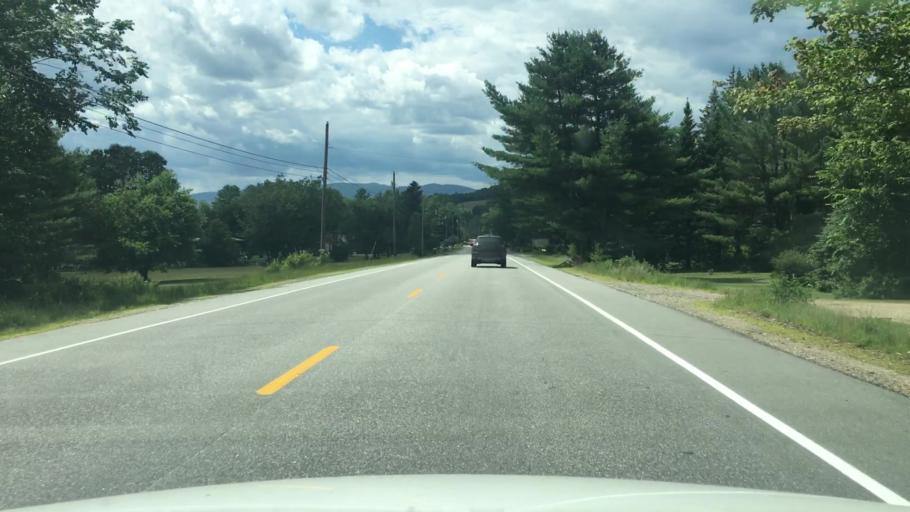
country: US
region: Maine
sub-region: Oxford County
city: Bethel
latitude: 44.4168
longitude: -70.7383
